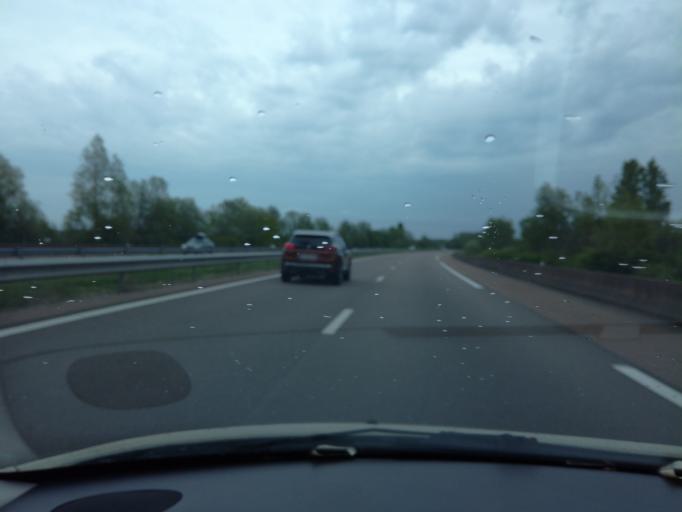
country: FR
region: Franche-Comte
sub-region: Departement du Jura
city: Choisey
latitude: 47.0378
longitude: 5.4590
